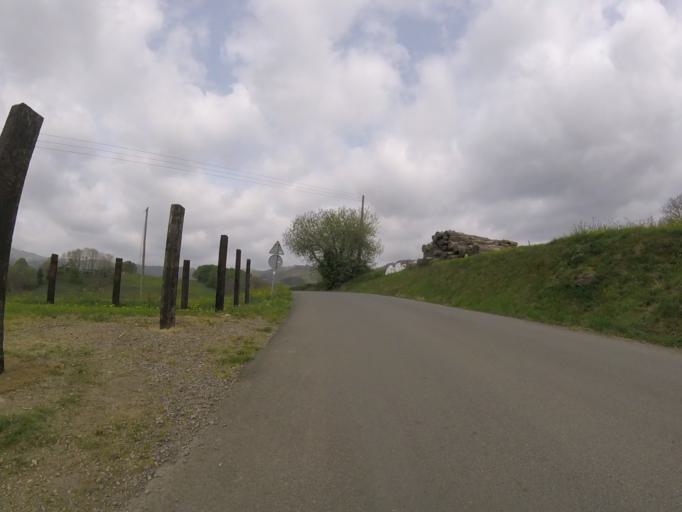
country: ES
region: Basque Country
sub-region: Provincia de Guipuzcoa
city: Zizurkil
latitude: 43.2010
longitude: -2.0753
